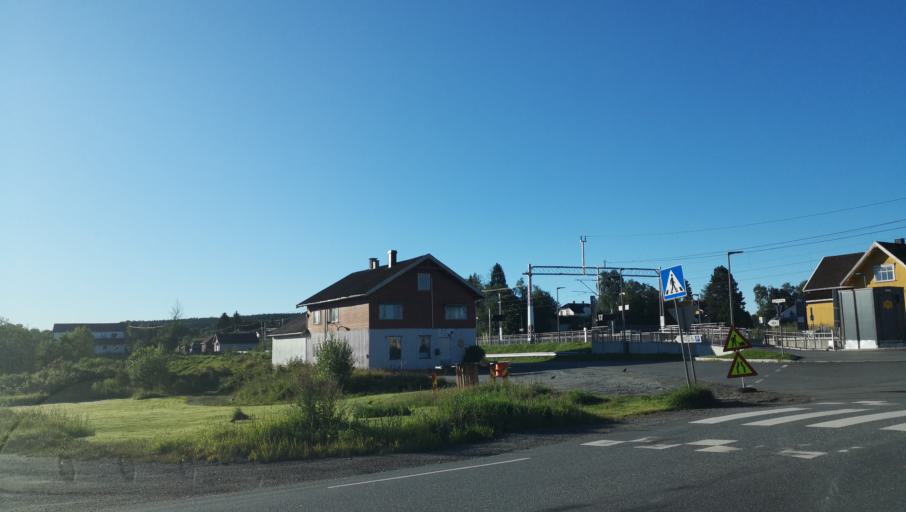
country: NO
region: Ostfold
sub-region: Hobol
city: Tomter
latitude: 59.6609
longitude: 11.0002
